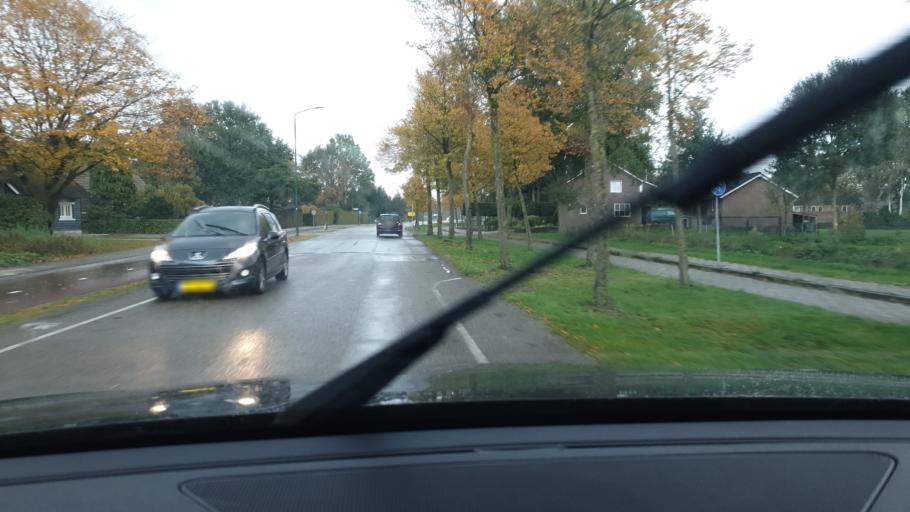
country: NL
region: North Brabant
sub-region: Gemeente Bernheze
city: Heesch
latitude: 51.6987
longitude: 5.5696
